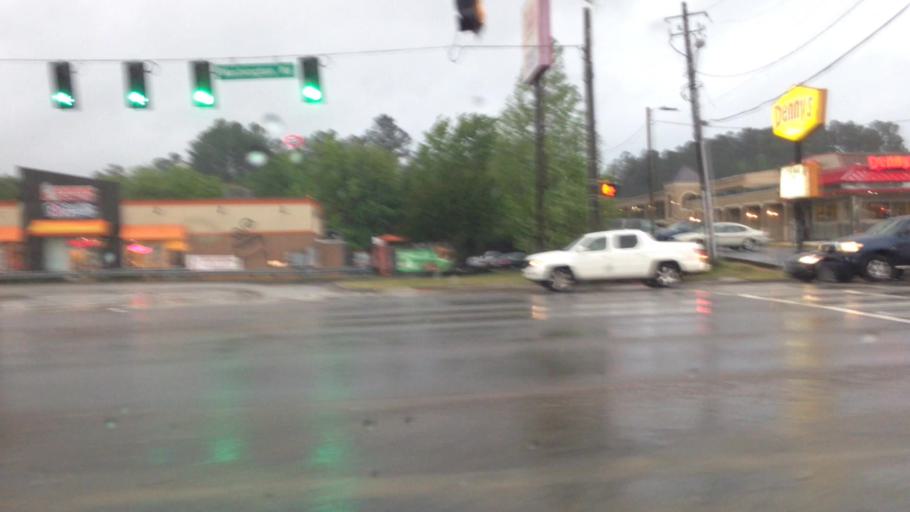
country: US
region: Georgia
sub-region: Columbia County
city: Martinez
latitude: 33.5127
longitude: -82.0463
